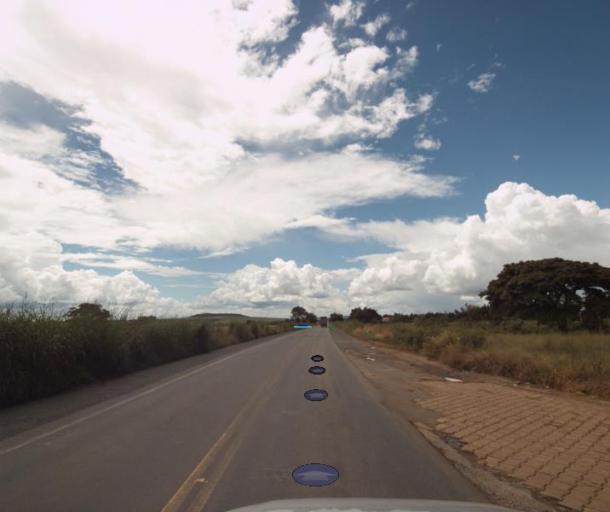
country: BR
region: Goias
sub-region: Uruacu
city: Uruacu
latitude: -14.1609
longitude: -49.1229
